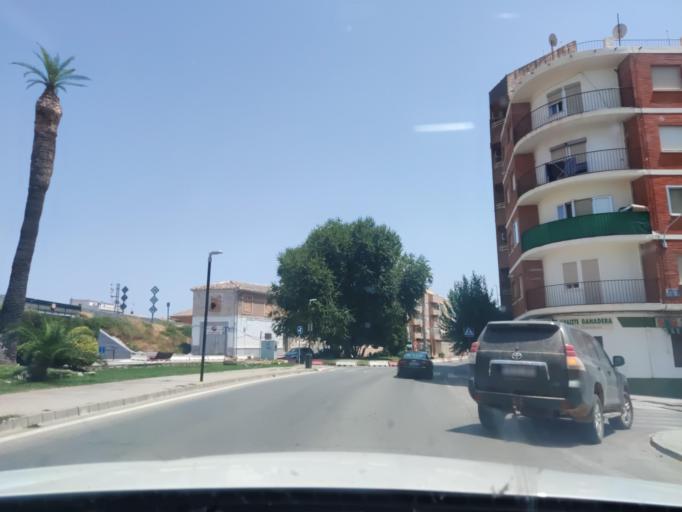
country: ES
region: Castille-La Mancha
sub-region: Provincia de Albacete
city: Hellin
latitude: 38.5099
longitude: -1.6929
